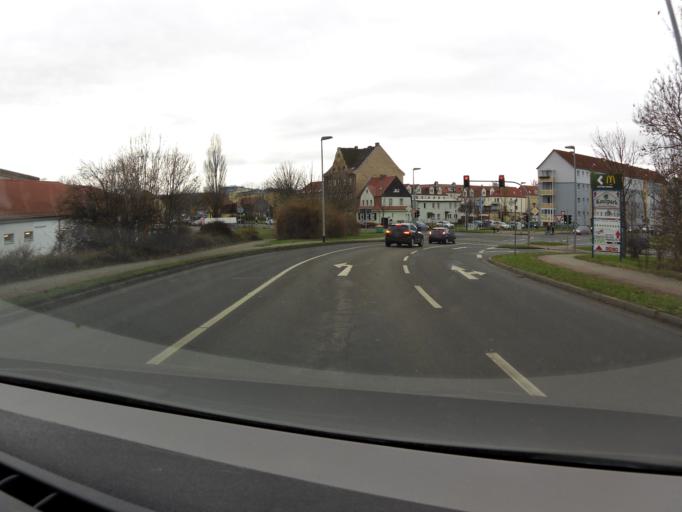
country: DE
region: Saxony-Anhalt
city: Aschersleben
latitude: 51.7633
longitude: 11.4503
